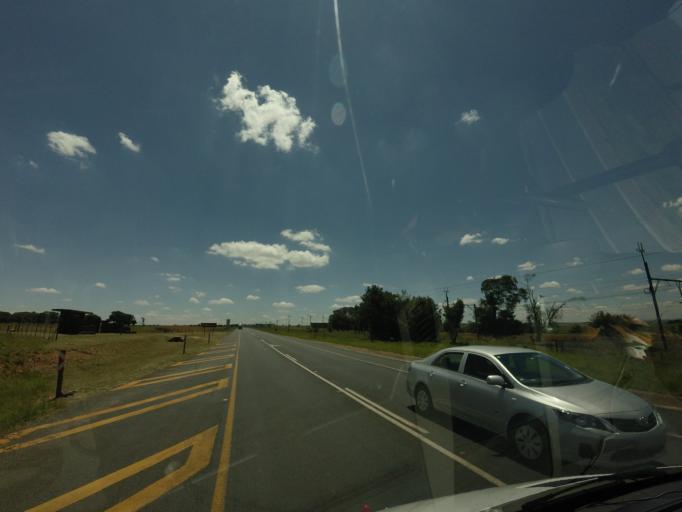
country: ZA
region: Mpumalanga
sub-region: Nkangala District Municipality
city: Belfast
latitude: -25.7324
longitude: 30.1048
